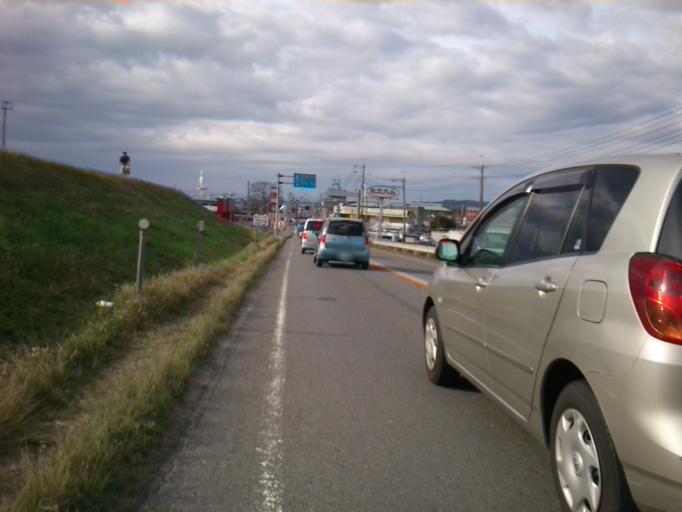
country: JP
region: Kyoto
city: Tanabe
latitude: 34.8240
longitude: 135.7944
